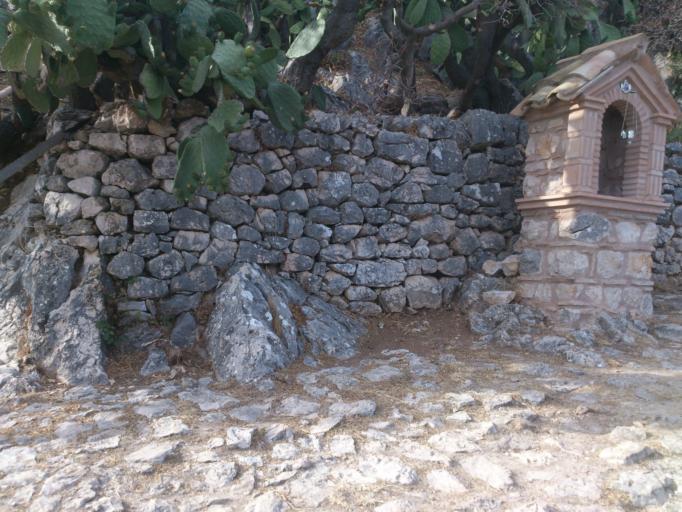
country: IT
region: Calabria
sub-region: Provincia di Reggio Calabria
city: Pazzano
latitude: 38.4678
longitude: 16.4488
